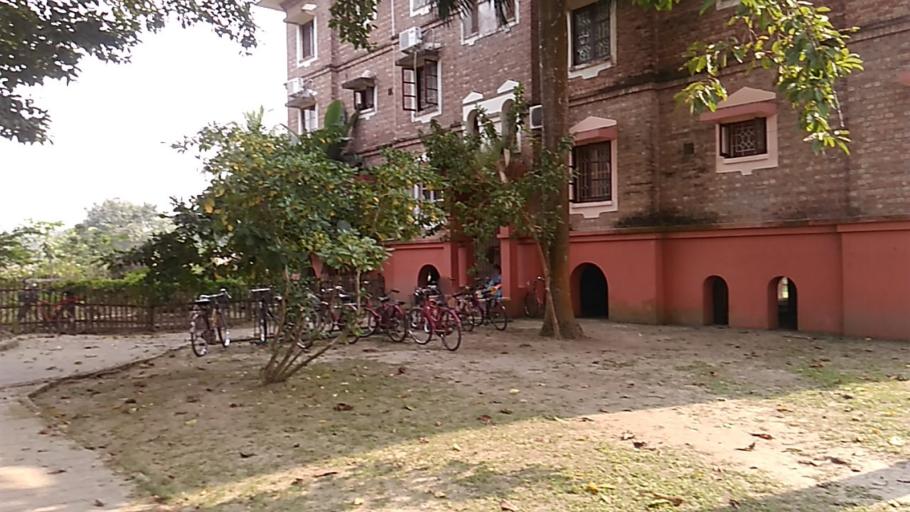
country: IN
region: West Bengal
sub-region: Nadia
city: Navadwip
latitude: 23.4218
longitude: 88.3885
